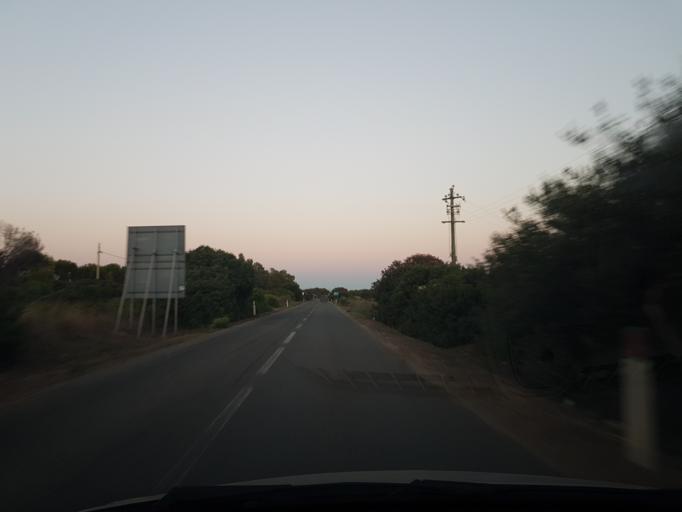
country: IT
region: Sardinia
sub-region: Provincia di Oristano
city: Riola Sardo
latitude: 40.0292
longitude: 8.4196
